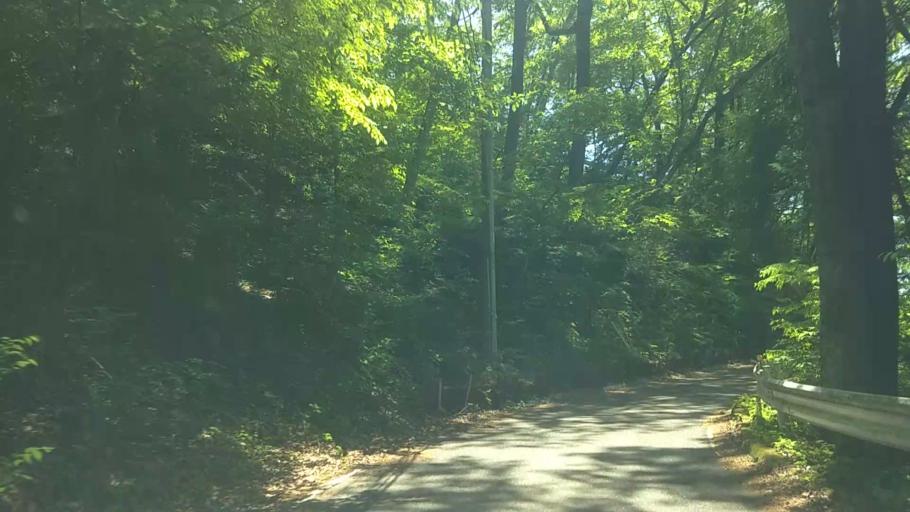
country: JP
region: Yamanashi
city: Nirasaki
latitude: 35.8757
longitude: 138.4326
